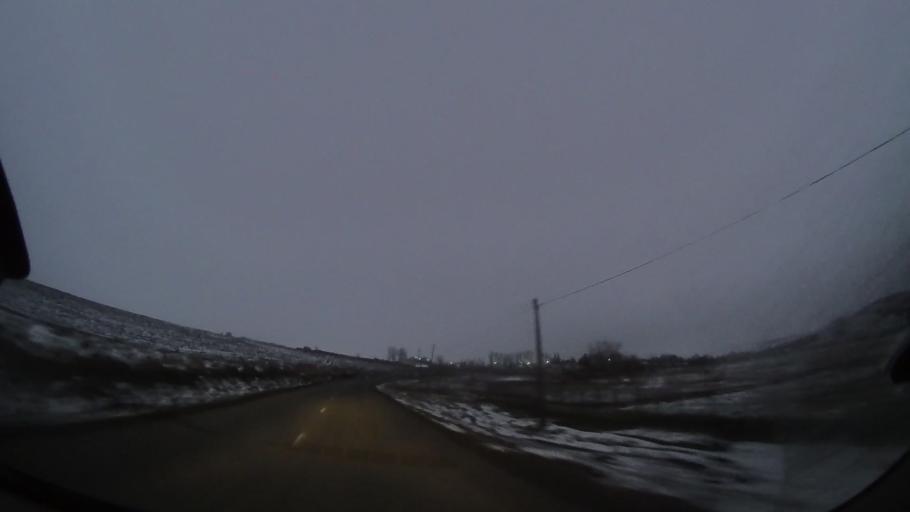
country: RO
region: Vaslui
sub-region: Comuna Dimitrie Cantemir
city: Dimitrie Cantemir
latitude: 46.4946
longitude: 28.0530
